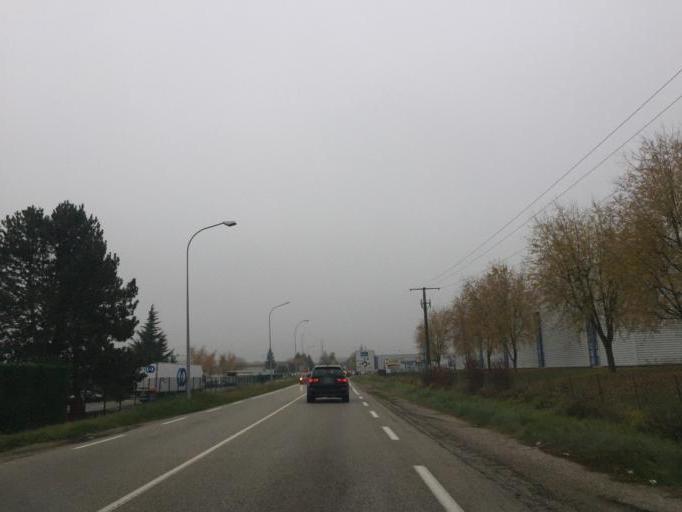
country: FR
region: Rhone-Alpes
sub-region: Departement de l'Ain
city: Mionnay
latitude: 45.8655
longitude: 4.9124
